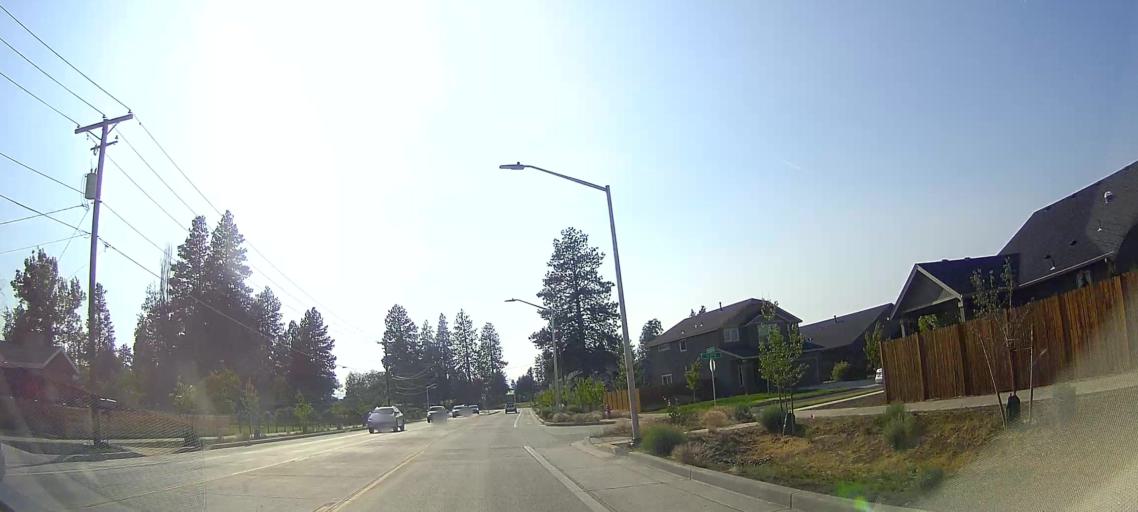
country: US
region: Oregon
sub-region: Deschutes County
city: Bend
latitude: 44.0385
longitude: -121.2969
